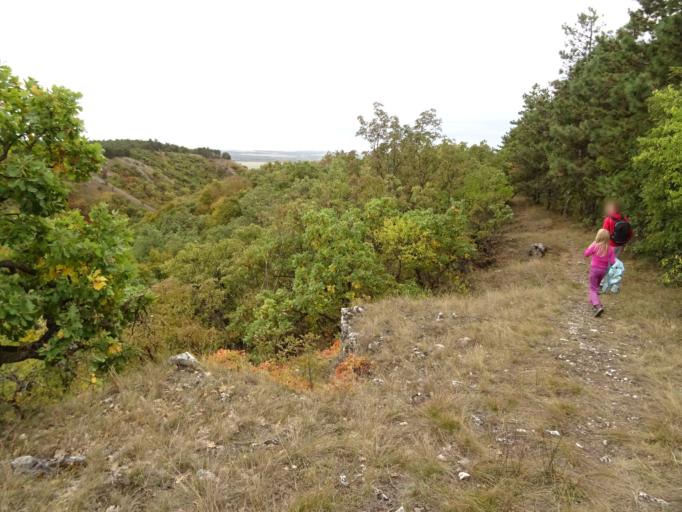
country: HU
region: Fejer
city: Kincsesbanya
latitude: 47.2190
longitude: 18.2431
